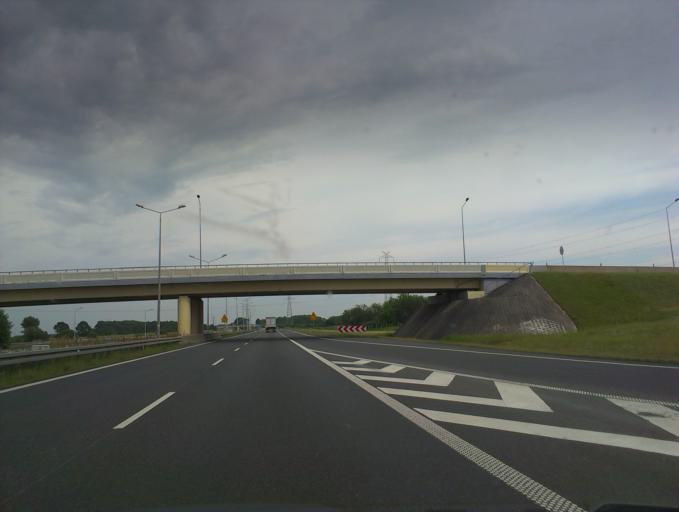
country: PL
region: Opole Voivodeship
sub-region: Powiat brzeski
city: Grodkow
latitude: 50.7815
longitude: 17.3496
